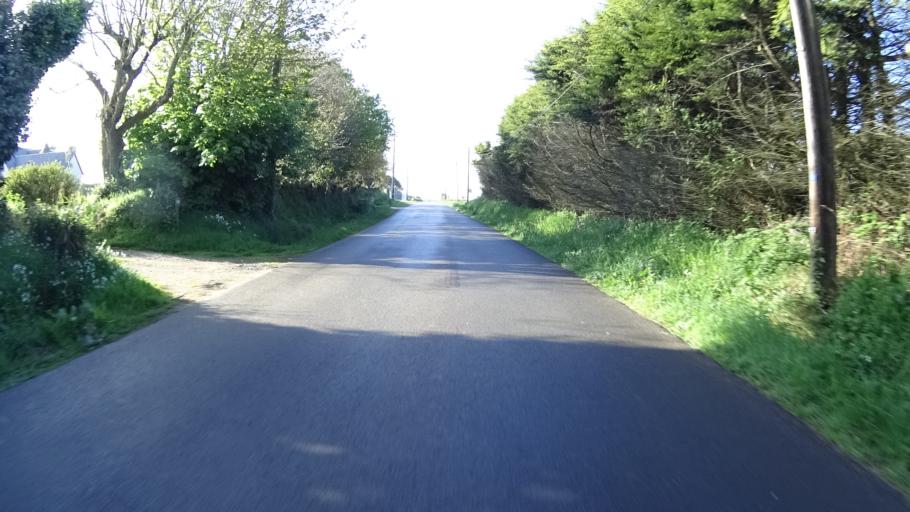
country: FR
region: Brittany
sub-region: Departement du Finistere
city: Plouarzel
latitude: 48.4327
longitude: -4.7155
